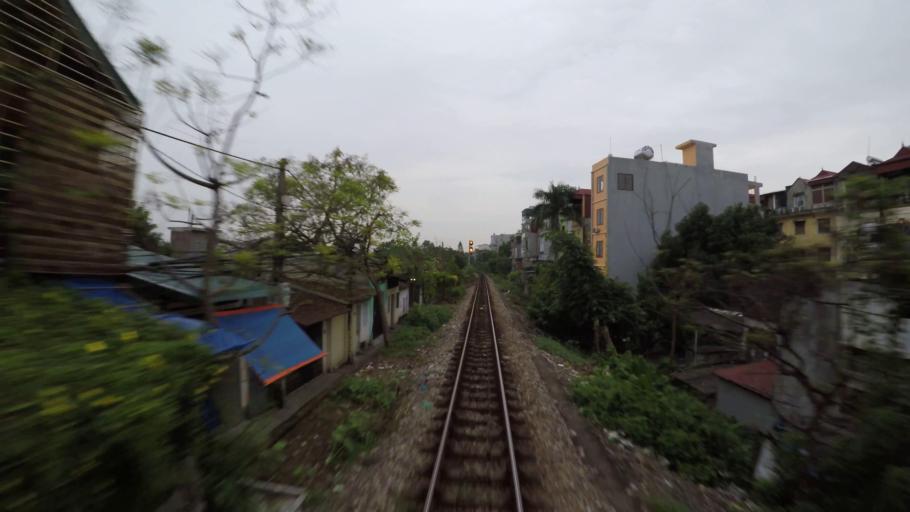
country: VN
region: Ha Noi
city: Trau Quy
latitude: 21.0404
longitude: 105.8974
